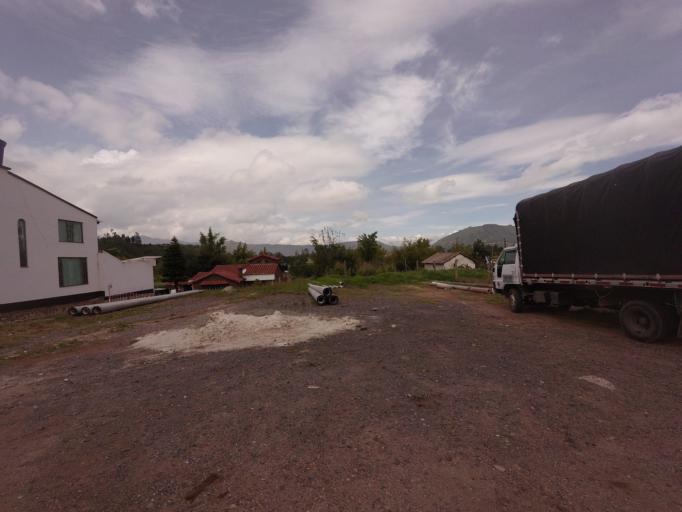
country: CO
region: Boyaca
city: Nobsa
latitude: 5.7851
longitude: -72.9718
